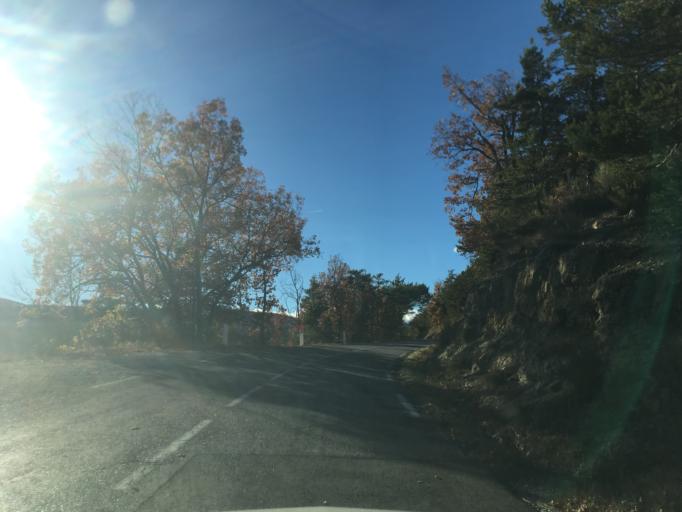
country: FR
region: Provence-Alpes-Cote d'Azur
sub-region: Departement des Alpes-de-Haute-Provence
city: Castellane
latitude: 43.7412
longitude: 6.4925
